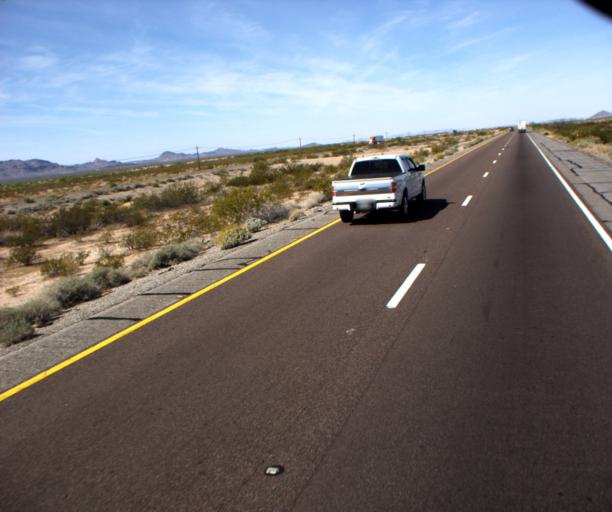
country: US
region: Arizona
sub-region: La Paz County
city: Salome
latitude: 33.5646
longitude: -113.3221
